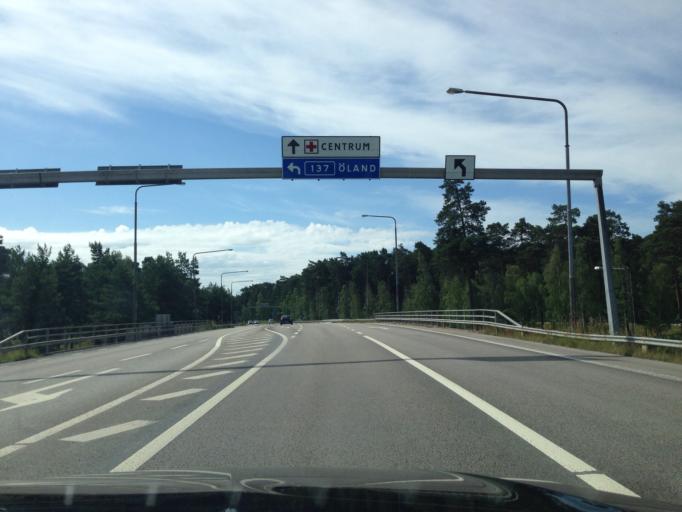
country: SE
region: Kalmar
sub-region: Kalmar Kommun
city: Kalmar
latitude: 56.6853
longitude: 16.3553
